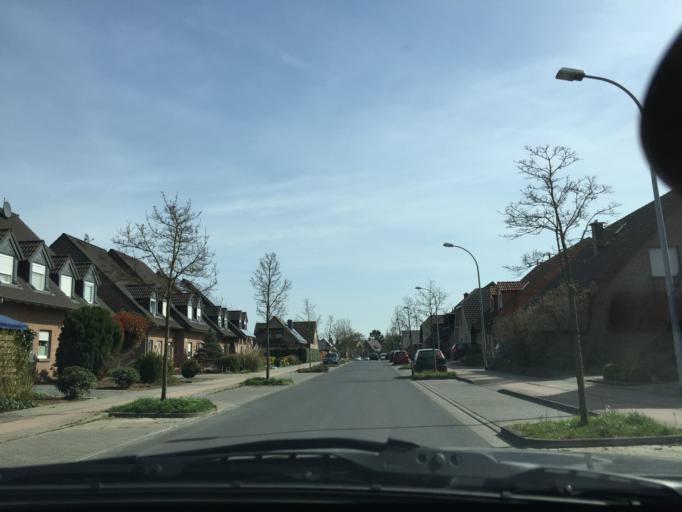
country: DE
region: North Rhine-Westphalia
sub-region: Regierungsbezirk Dusseldorf
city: Goch
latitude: 51.6669
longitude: 6.1564
